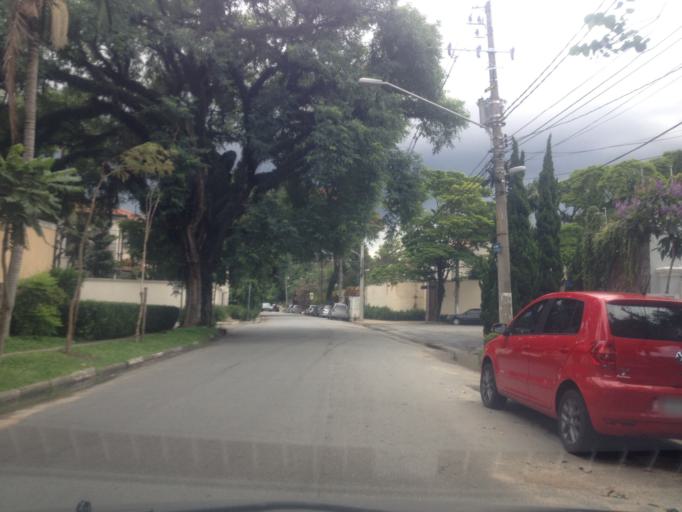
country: BR
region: Sao Paulo
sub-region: Sao Paulo
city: Sao Paulo
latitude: -23.5773
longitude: -46.6782
